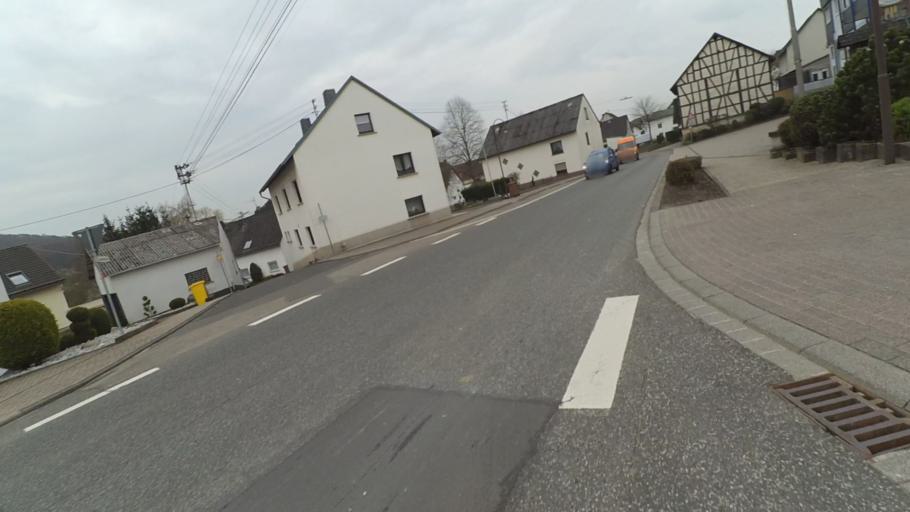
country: DE
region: Rheinland-Pfalz
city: Leuterod
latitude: 50.4939
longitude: 7.8208
